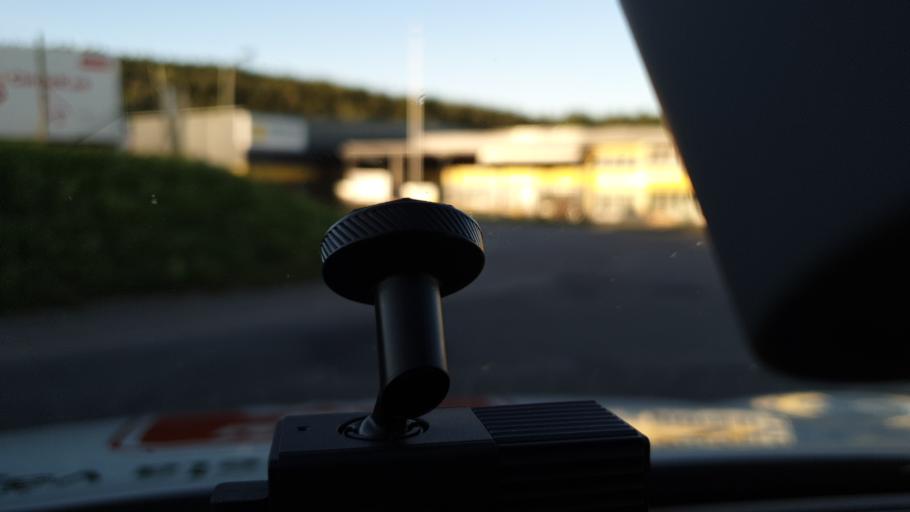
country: SE
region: Vaesternorrland
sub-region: Sundsvalls Kommun
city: Johannedal
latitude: 62.4136
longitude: 17.3490
